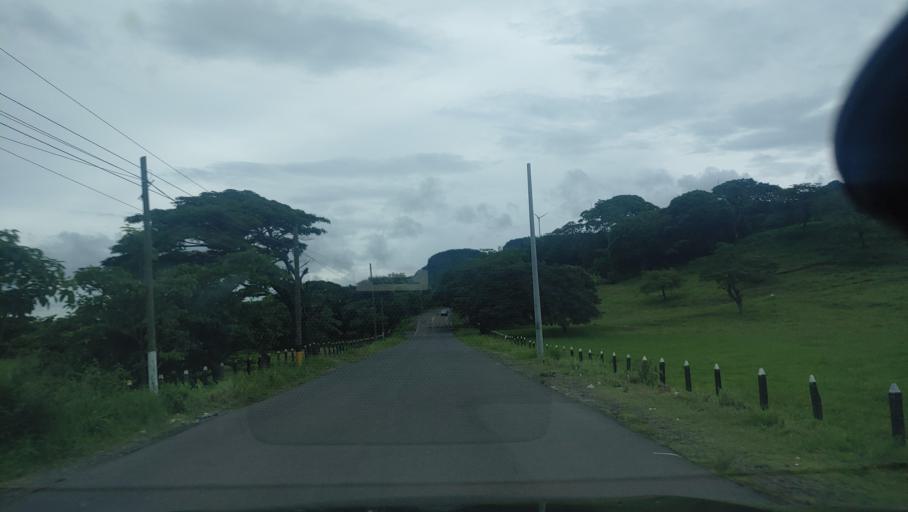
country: HN
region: Choluteca
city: Corpus
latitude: 13.3633
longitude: -86.9790
